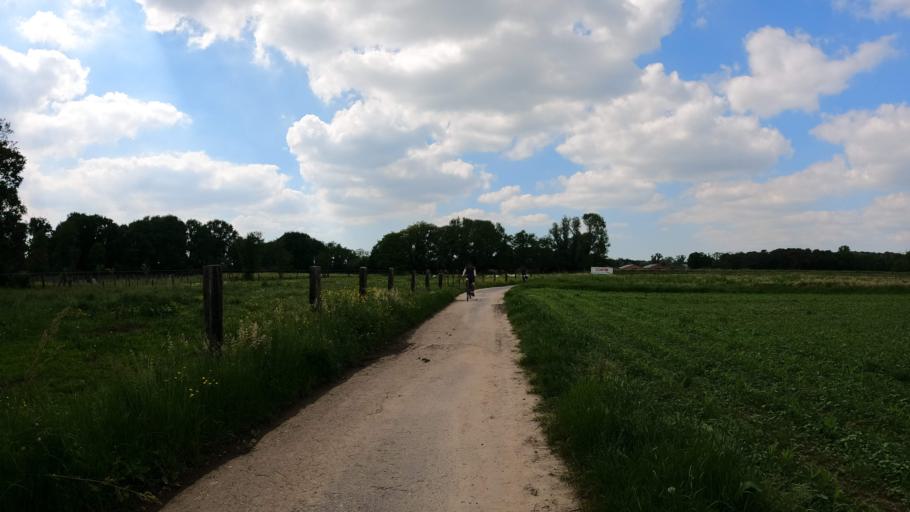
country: BE
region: Flanders
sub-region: Provincie Vlaams-Brabant
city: Keerbergen
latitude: 50.9914
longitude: 4.6193
